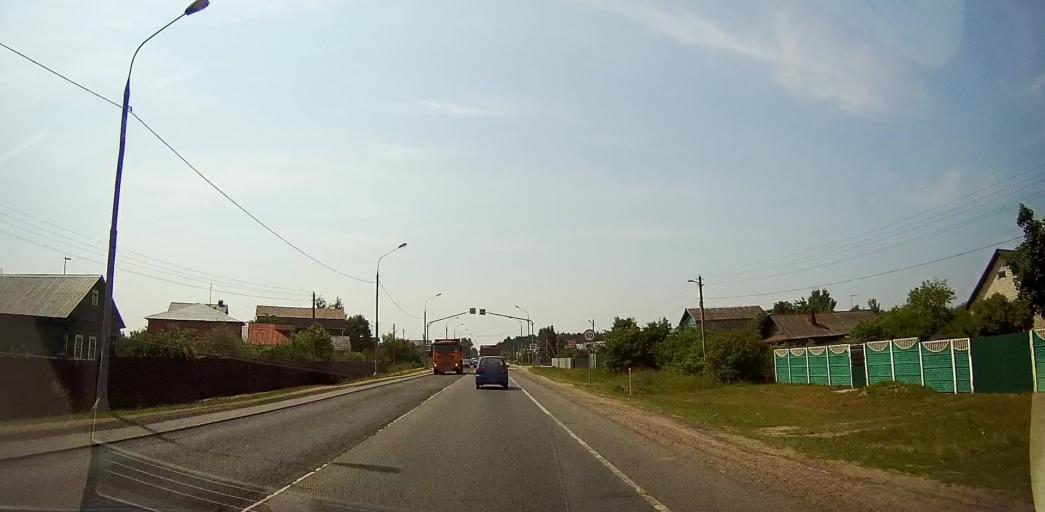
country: RU
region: Moskovskaya
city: Malyshevo
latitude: 55.4681
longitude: 38.3393
